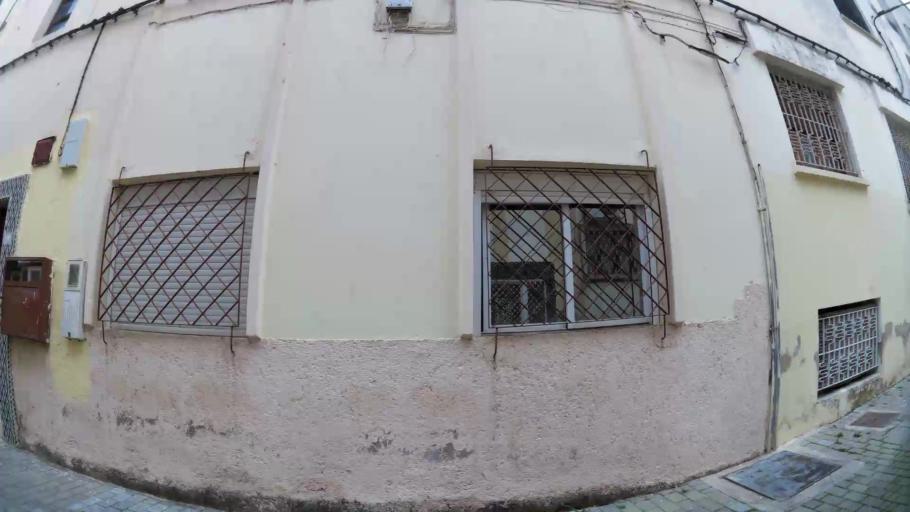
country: MA
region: Fes-Boulemane
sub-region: Fes
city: Fes
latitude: 34.0362
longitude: -5.0177
